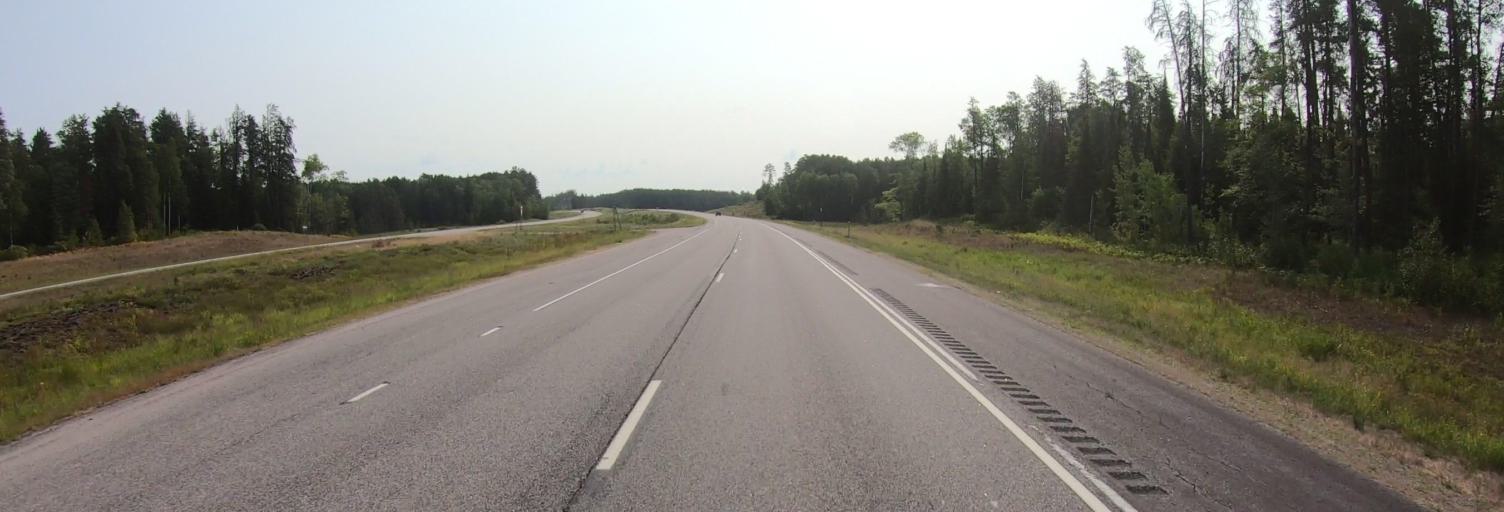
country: US
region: Minnesota
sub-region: Saint Louis County
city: Mountain Iron
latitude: 47.6599
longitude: -92.6173
